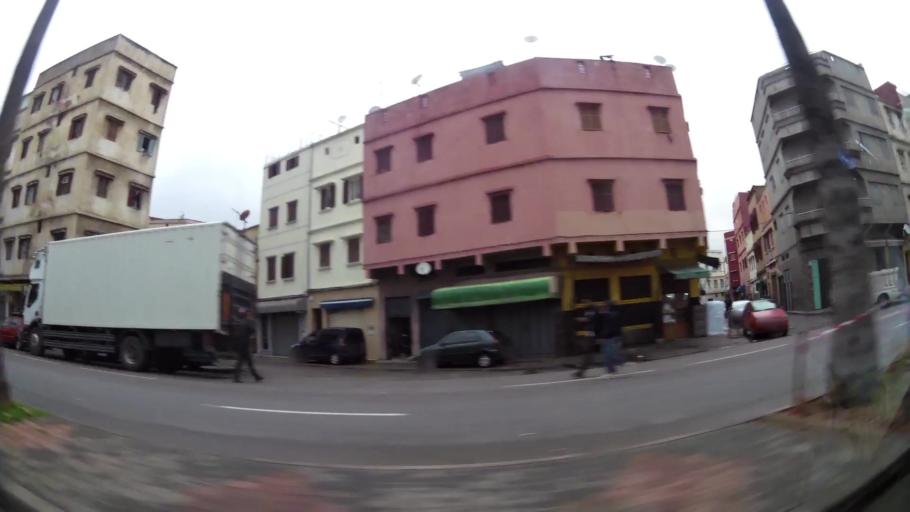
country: MA
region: Grand Casablanca
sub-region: Casablanca
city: Casablanca
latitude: 33.5627
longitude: -7.6046
